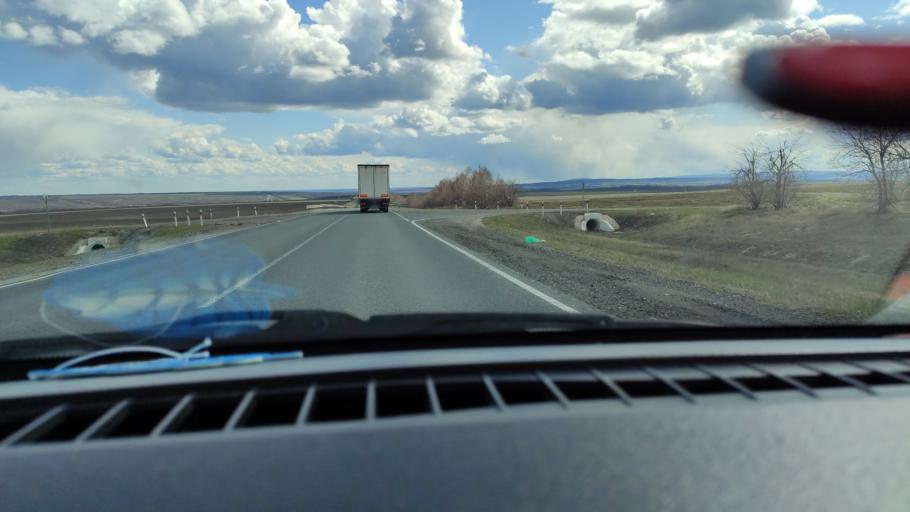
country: RU
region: Saratov
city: Dukhovnitskoye
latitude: 52.7864
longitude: 48.2331
